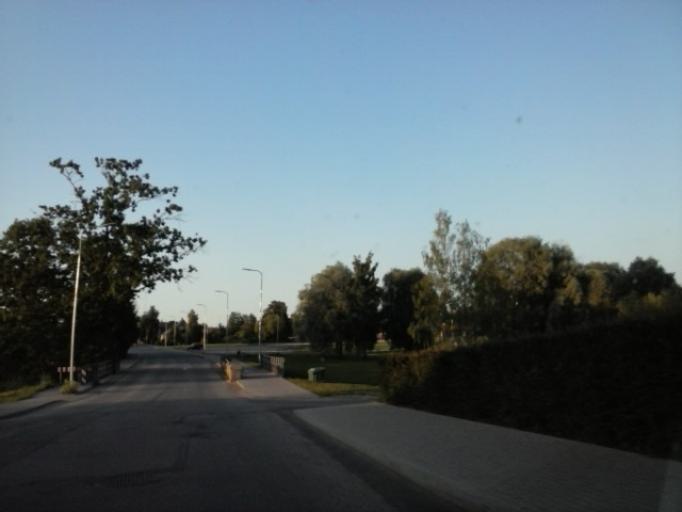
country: EE
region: Vorumaa
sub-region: Voru linn
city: Voru
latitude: 57.8495
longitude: 26.9991
